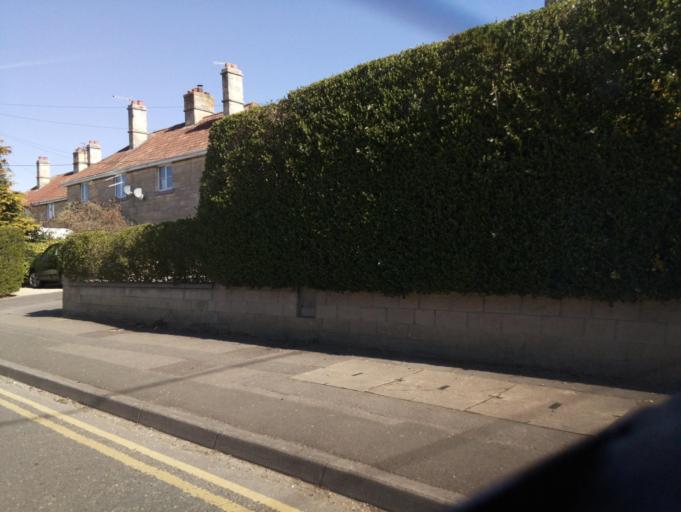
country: GB
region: England
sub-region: Wiltshire
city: Bradford-on-Avon
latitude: 51.3395
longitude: -2.2428
